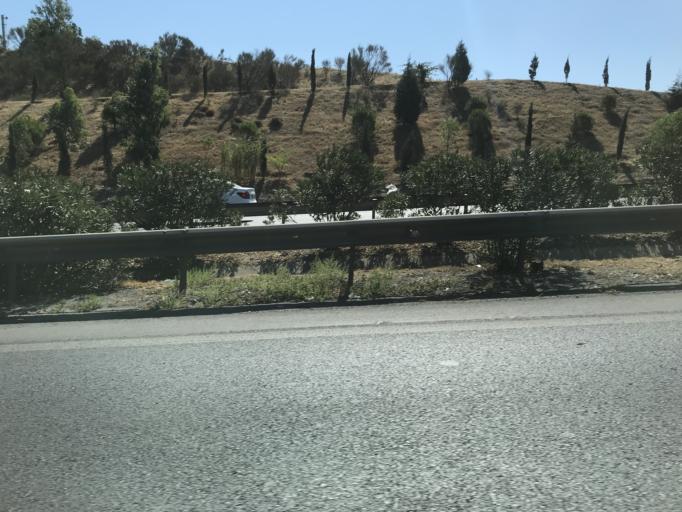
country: TR
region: Izmir
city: Buca
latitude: 38.4000
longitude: 27.2296
